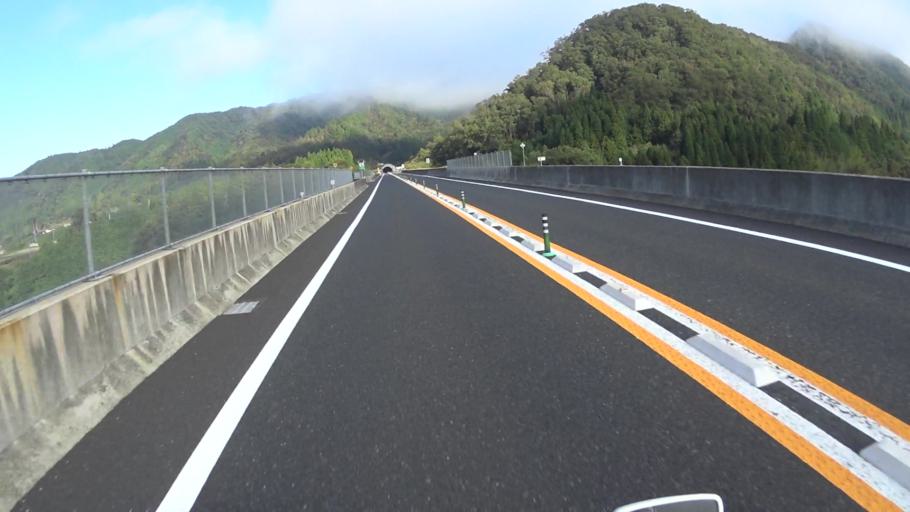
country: JP
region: Kyoto
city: Ayabe
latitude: 35.2959
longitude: 135.3339
